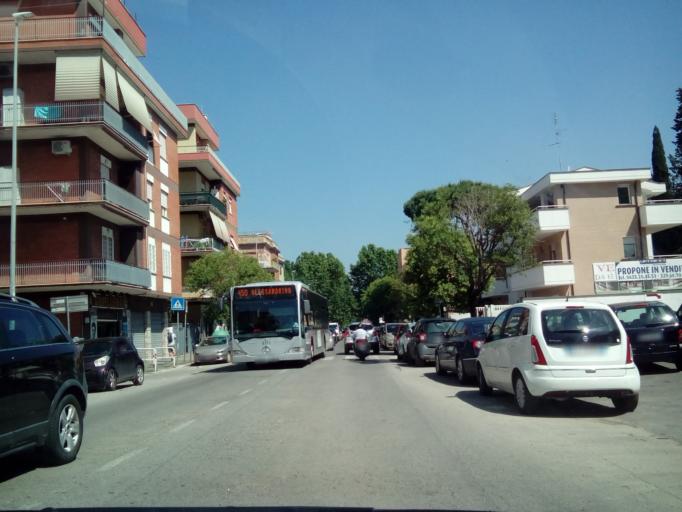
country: IT
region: Latium
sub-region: Citta metropolitana di Roma Capitale
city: Rome
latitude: 41.8778
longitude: 12.5785
